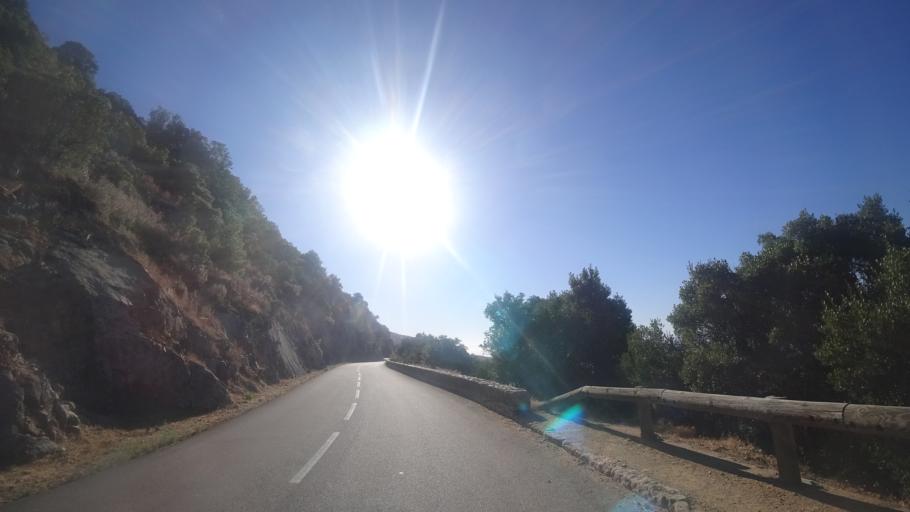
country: FR
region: Corsica
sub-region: Departement de la Corse-du-Sud
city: Cargese
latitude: 42.2405
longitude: 8.6474
